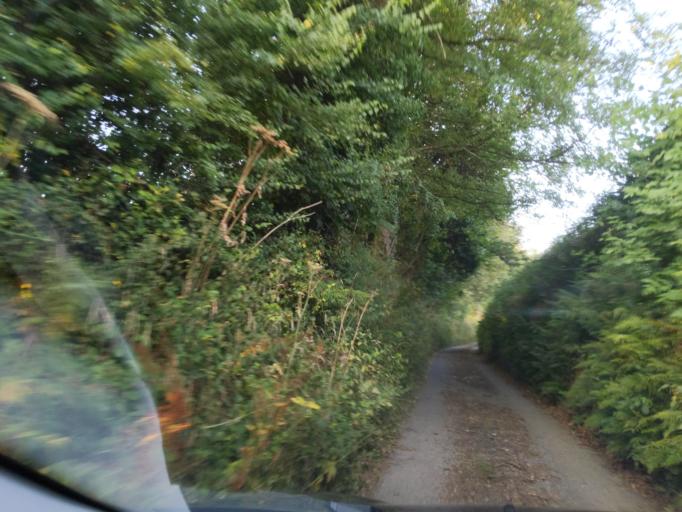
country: GB
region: England
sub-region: Cornwall
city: Fowey
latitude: 50.3658
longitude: -4.5934
